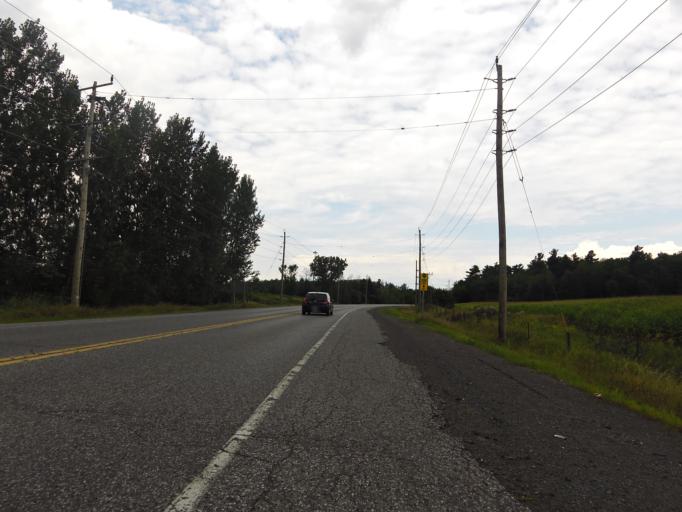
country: CA
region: Ontario
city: Bells Corners
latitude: 45.3187
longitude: -75.8035
